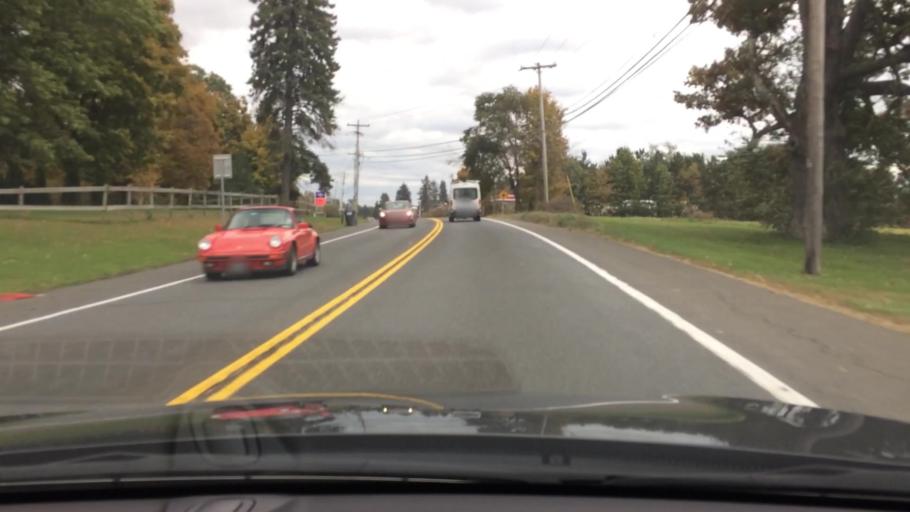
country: US
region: New York
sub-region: Columbia County
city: Niverville
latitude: 42.4540
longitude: -73.6951
